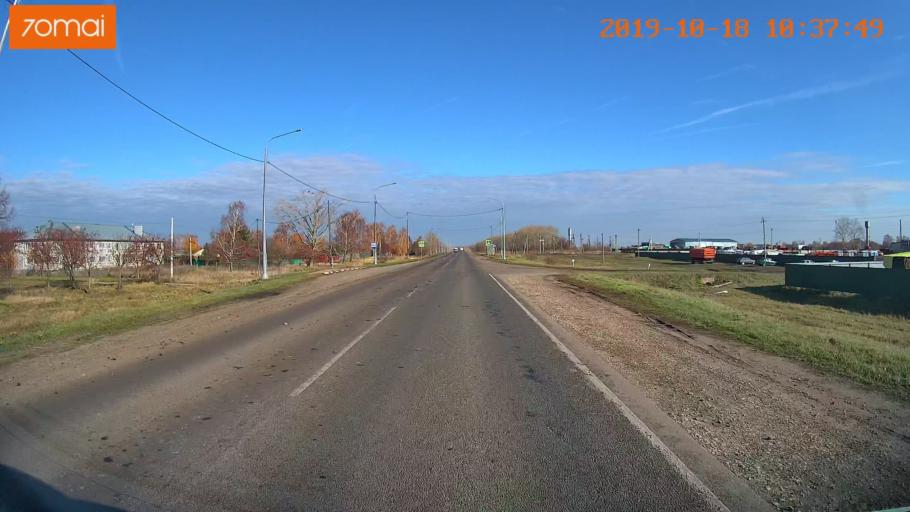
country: RU
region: Tula
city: Kurkino
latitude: 53.5652
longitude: 38.6350
